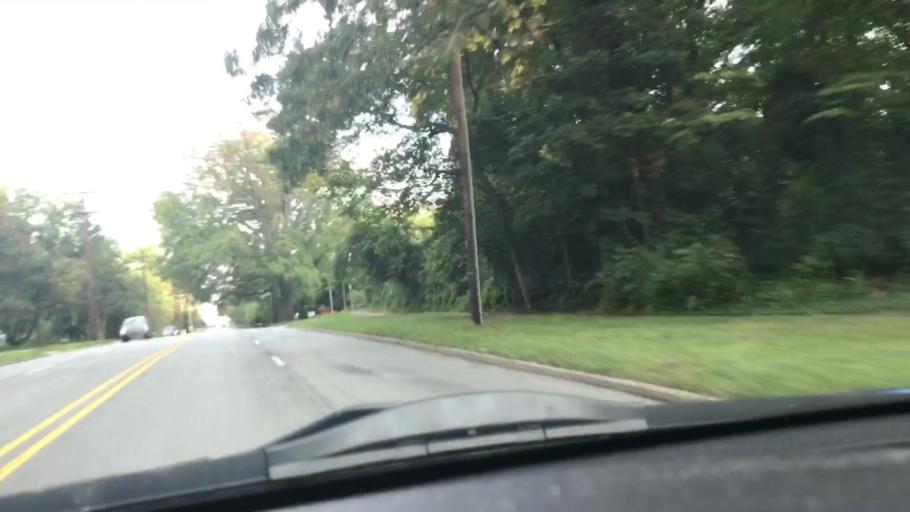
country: US
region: North Carolina
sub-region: Guilford County
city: Greensboro
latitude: 36.0786
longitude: -79.8228
